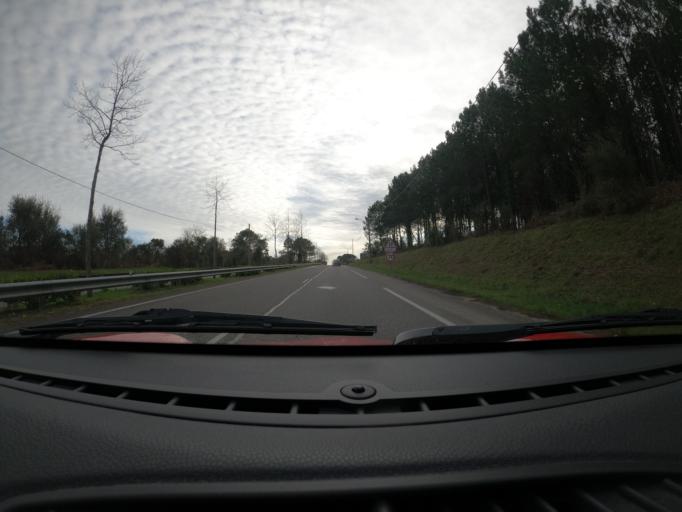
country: FR
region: Aquitaine
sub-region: Departement des Landes
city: Ondres
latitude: 43.5717
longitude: -1.4403
